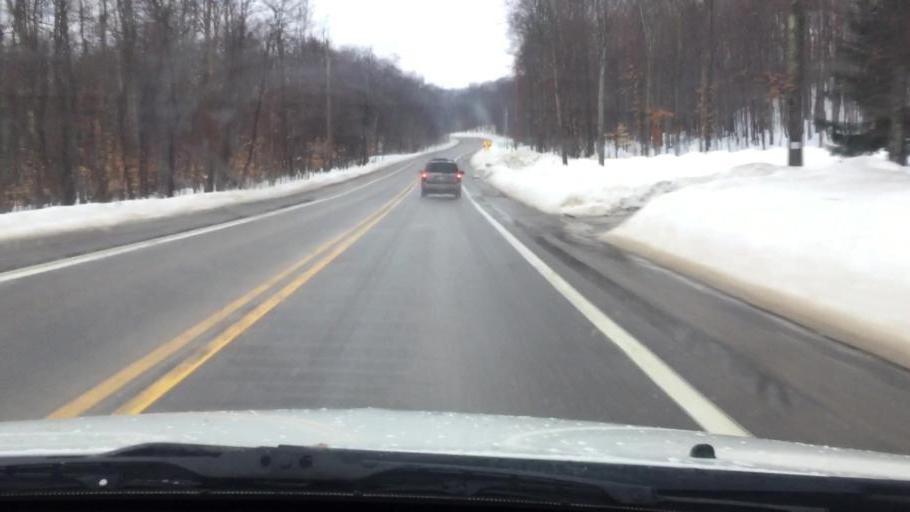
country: US
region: Michigan
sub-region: Charlevoix County
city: East Jordan
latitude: 45.2175
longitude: -85.1722
